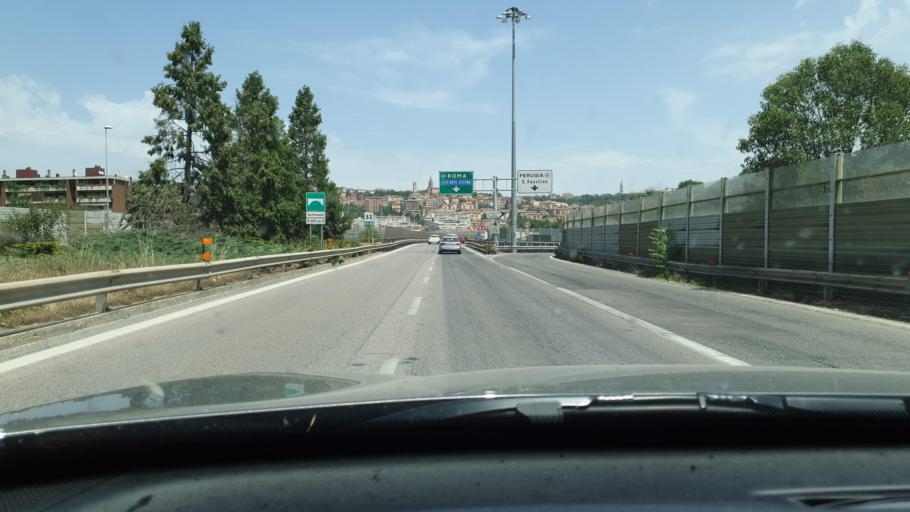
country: IT
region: Umbria
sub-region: Provincia di Perugia
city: Perugia
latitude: 43.0974
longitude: 12.3677
